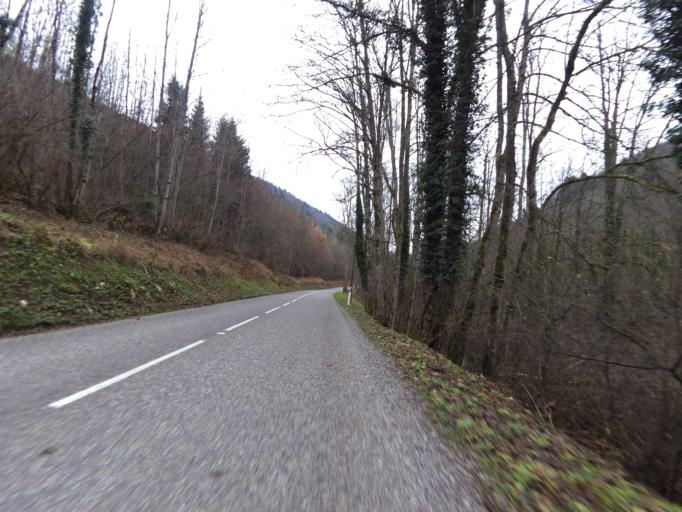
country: FR
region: Alsace
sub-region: Departement du Haut-Rhin
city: Ferrette
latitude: 47.4394
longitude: 7.3033
